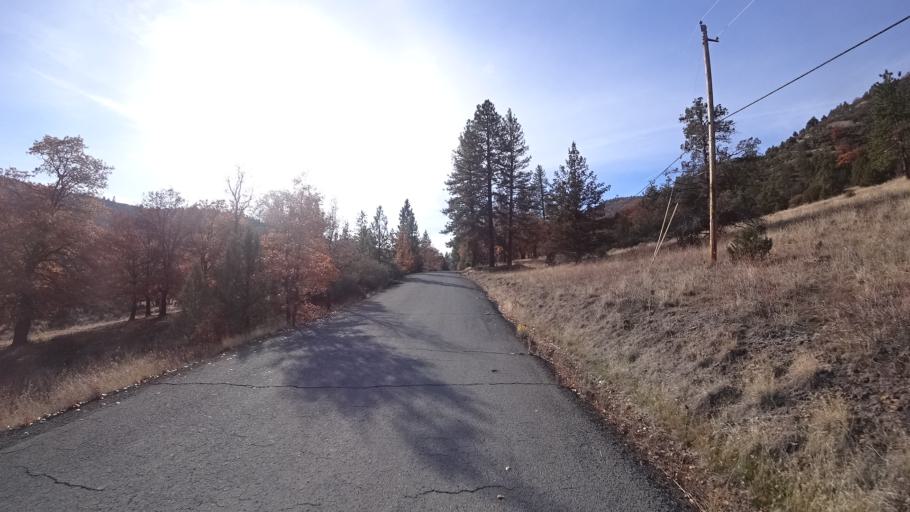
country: US
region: California
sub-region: Siskiyou County
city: Montague
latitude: 41.6180
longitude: -122.5780
